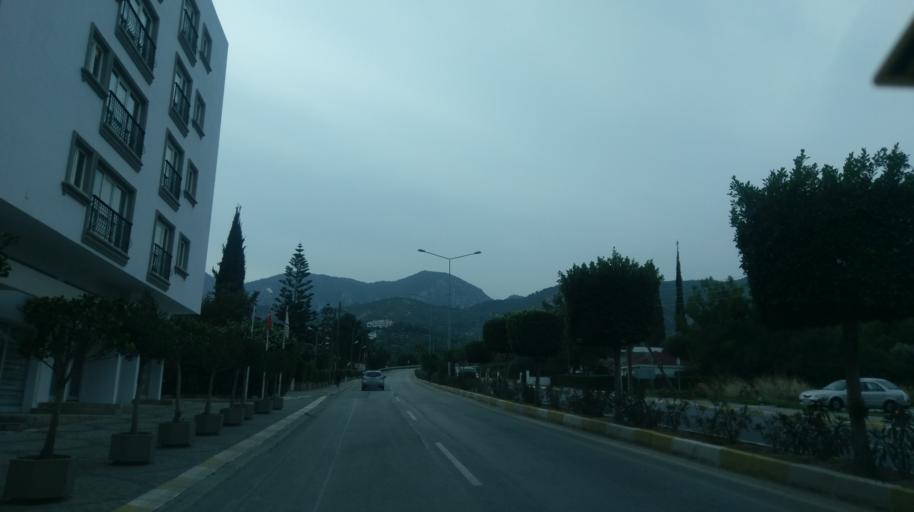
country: CY
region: Keryneia
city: Kyrenia
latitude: 35.3278
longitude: 33.3190
